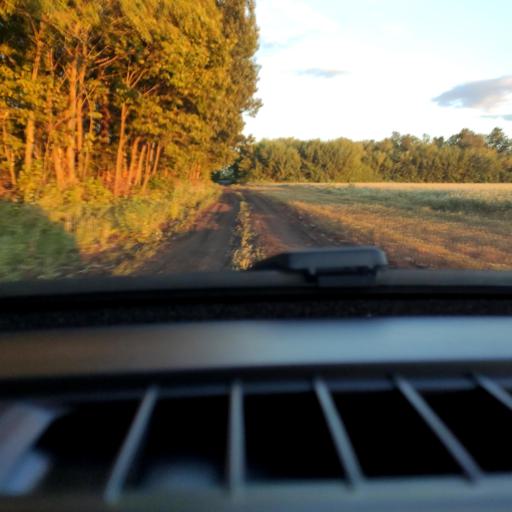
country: RU
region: Voronezj
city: Panino
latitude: 51.5654
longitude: 39.8880
